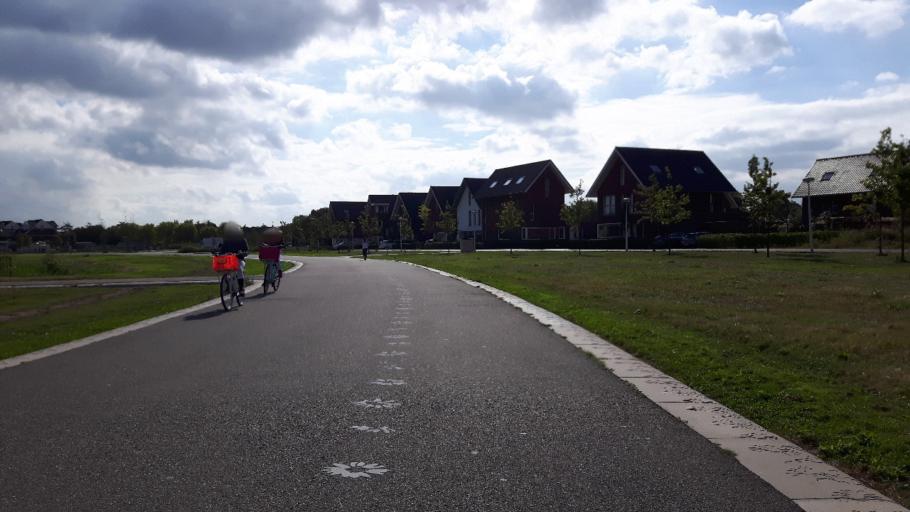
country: NL
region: Utrecht
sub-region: Stichtse Vecht
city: Spechtenkamp
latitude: 52.0903
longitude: 5.0260
